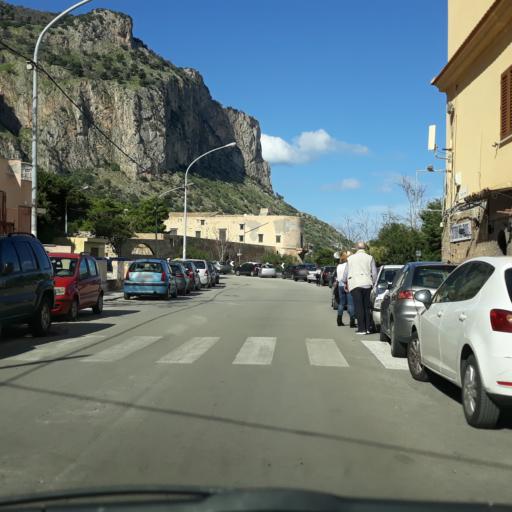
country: IT
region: Sicily
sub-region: Palermo
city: Palermo
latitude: 38.1647
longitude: 13.3693
